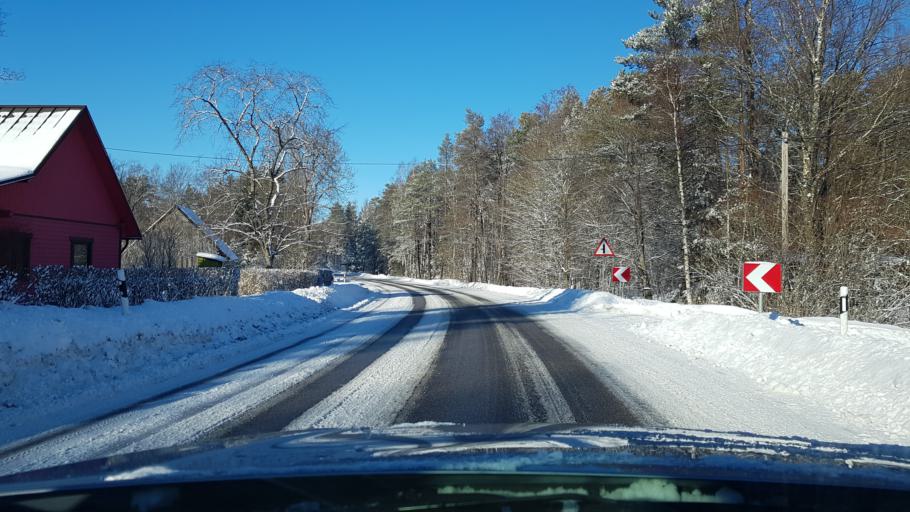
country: EE
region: Hiiumaa
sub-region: Kaerdla linn
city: Kardla
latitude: 58.9219
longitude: 22.7941
